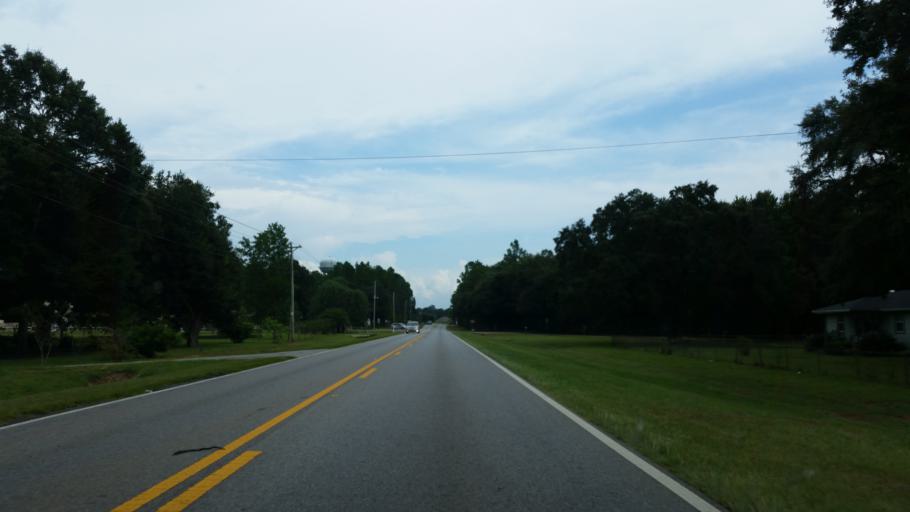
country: US
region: Florida
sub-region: Santa Rosa County
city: Wallace
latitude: 30.6636
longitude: -87.2022
